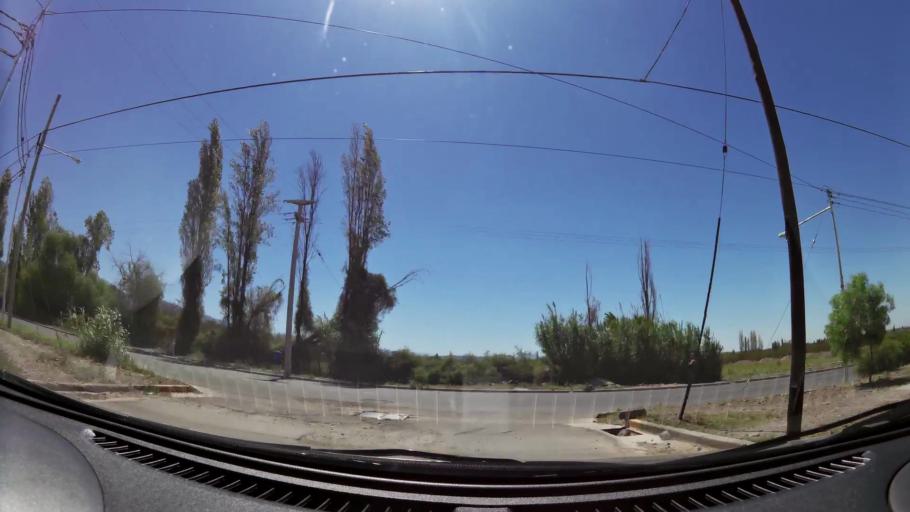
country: AR
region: Mendoza
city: Las Heras
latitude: -32.8464
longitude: -68.8576
